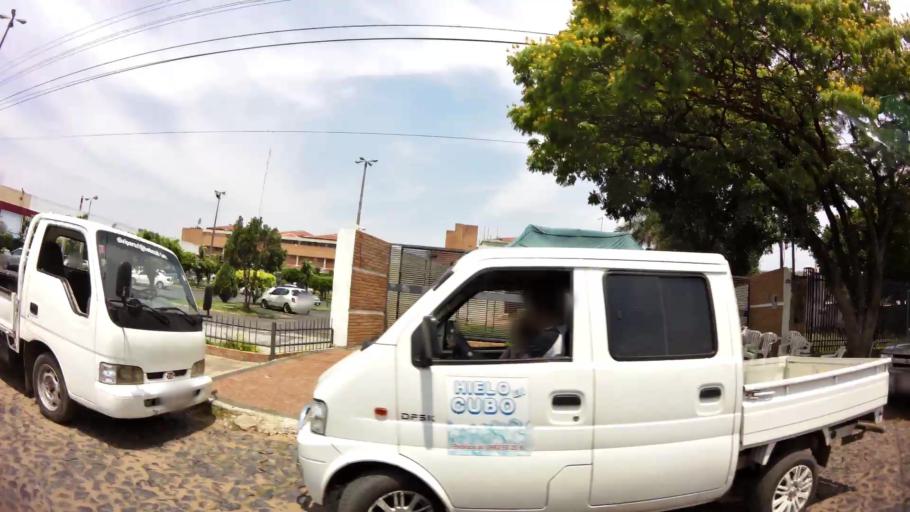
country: PY
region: Central
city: Lambare
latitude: -25.3153
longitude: -57.5705
